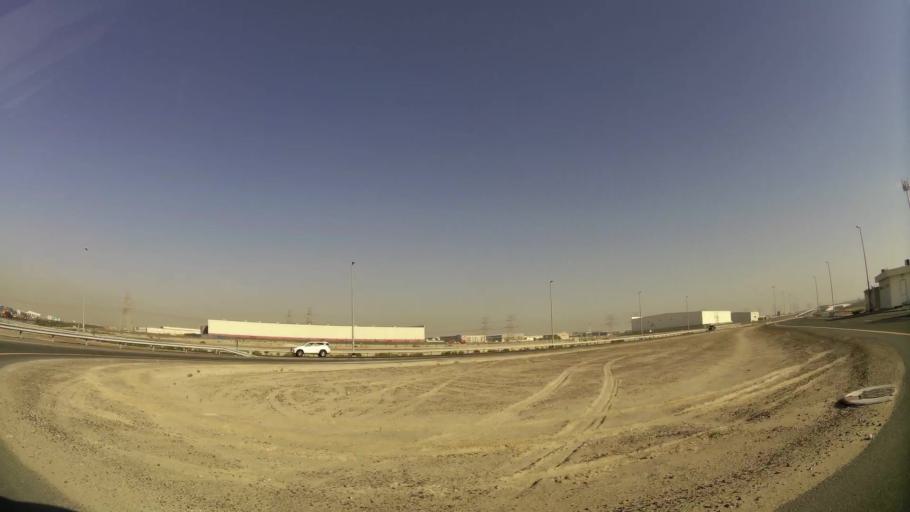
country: AE
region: Dubai
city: Dubai
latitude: 24.9804
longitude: 55.1143
